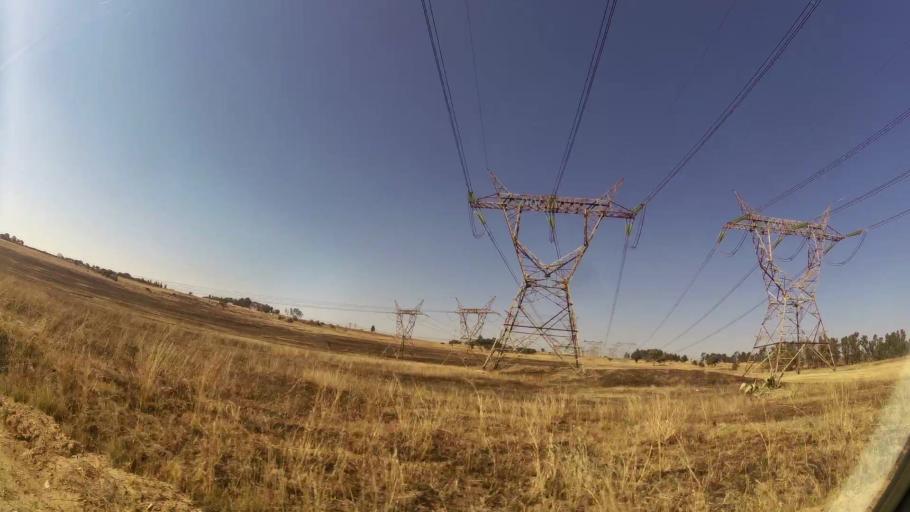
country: ZA
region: Gauteng
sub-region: City of Johannesburg Metropolitan Municipality
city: Diepsloot
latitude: -25.9086
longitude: 28.0707
